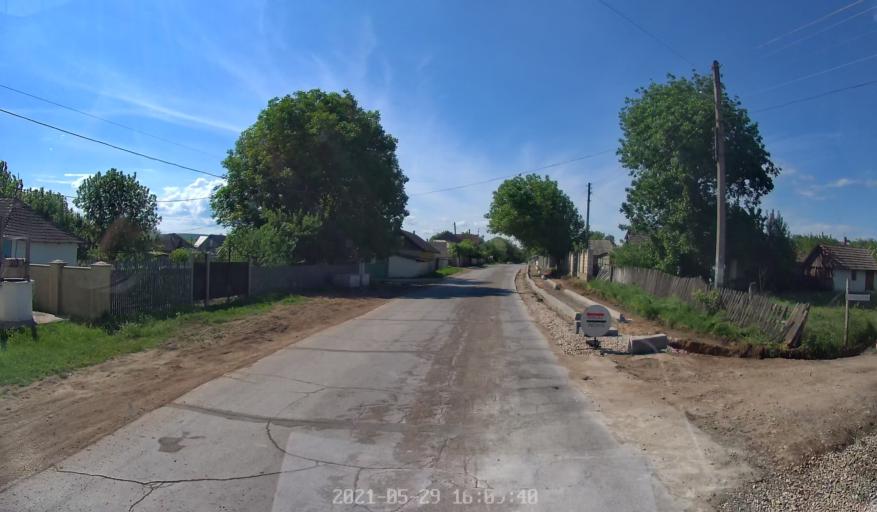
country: MD
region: Chisinau
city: Singera
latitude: 46.8210
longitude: 28.8807
